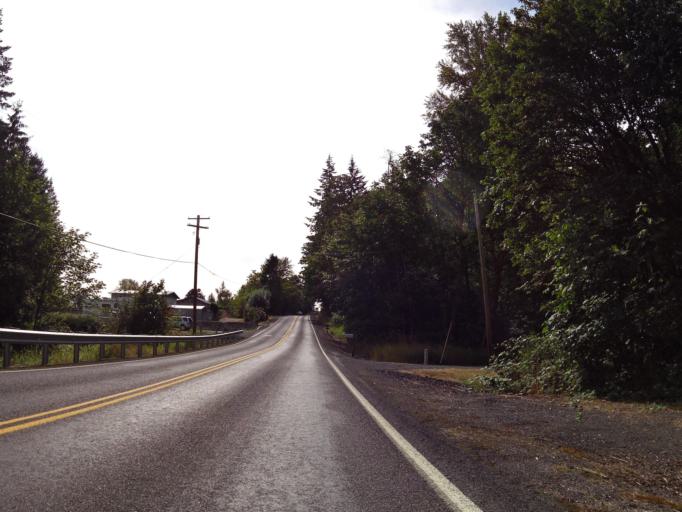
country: US
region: Washington
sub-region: Lewis County
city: Chehalis
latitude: 46.6307
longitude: -122.9689
